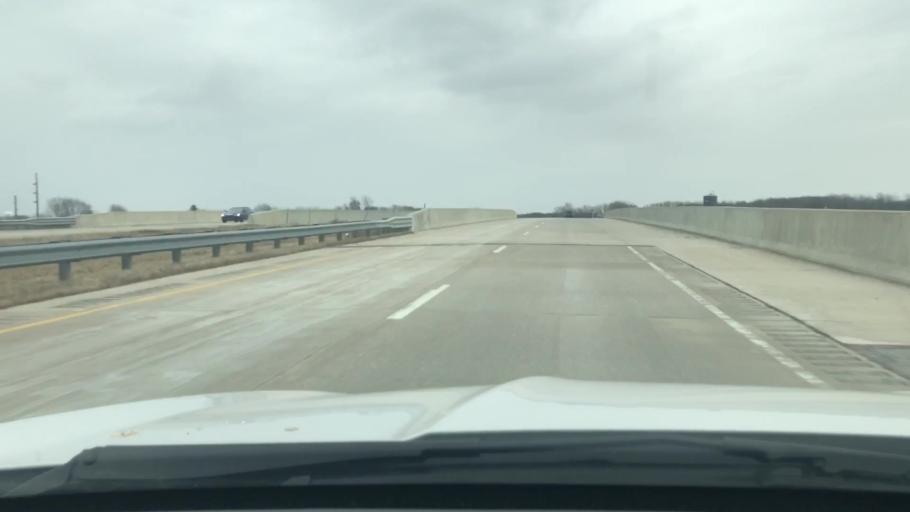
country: US
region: Indiana
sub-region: Cass County
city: Dunkirk
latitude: 40.7280
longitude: -86.4097
